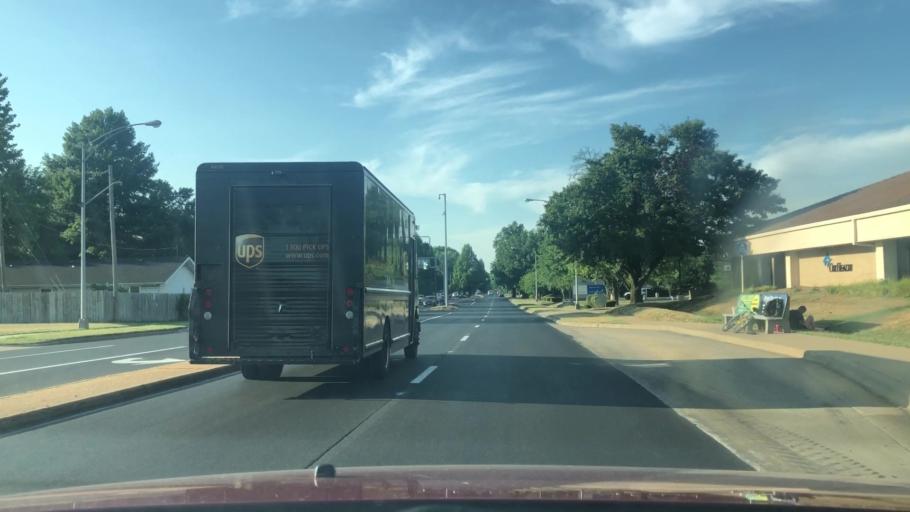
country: US
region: Missouri
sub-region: Greene County
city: Springfield
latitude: 37.1616
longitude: -93.2771
